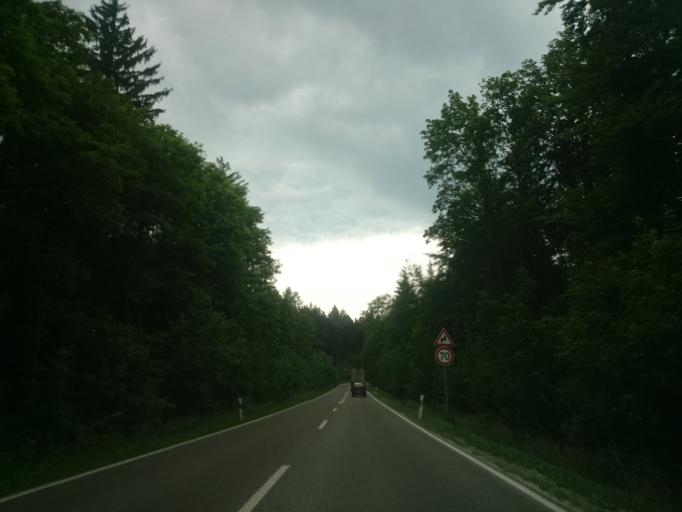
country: DE
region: Saxony
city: Lengefeld
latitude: 50.7011
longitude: 13.1701
